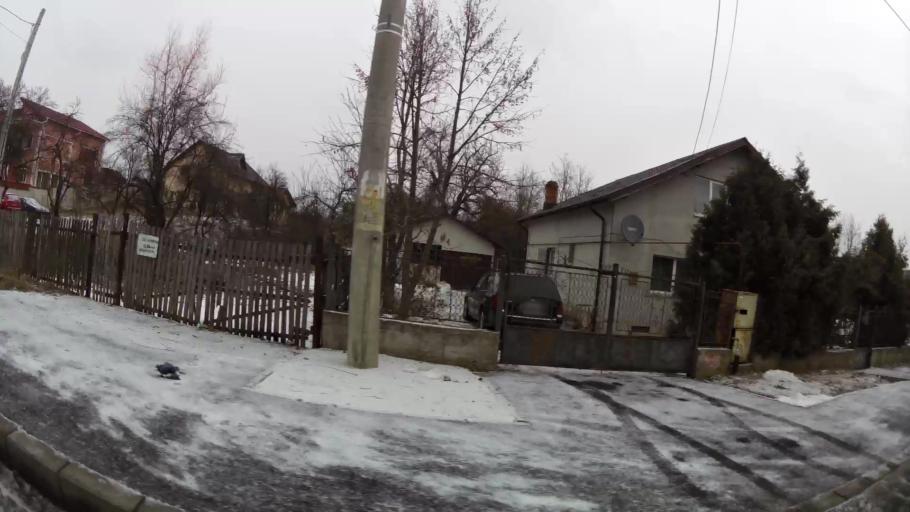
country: RO
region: Dambovita
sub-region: Municipiul Targoviste
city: Targoviste
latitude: 44.9381
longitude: 25.4675
